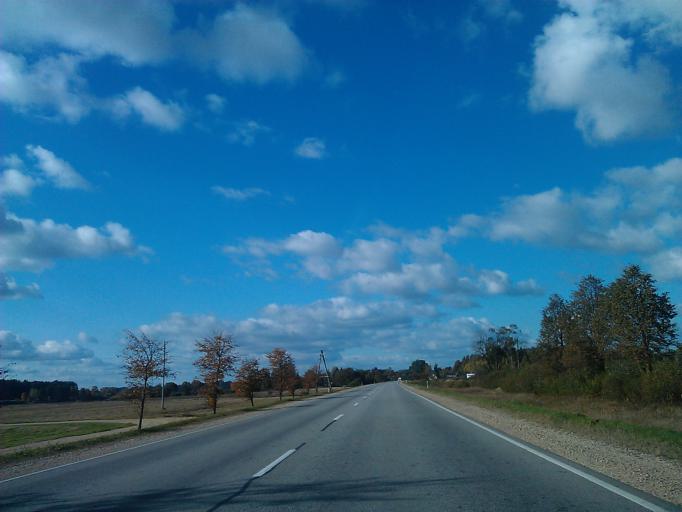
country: LV
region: Jekabpils Rajons
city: Jekabpils
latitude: 56.4853
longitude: 25.9233
